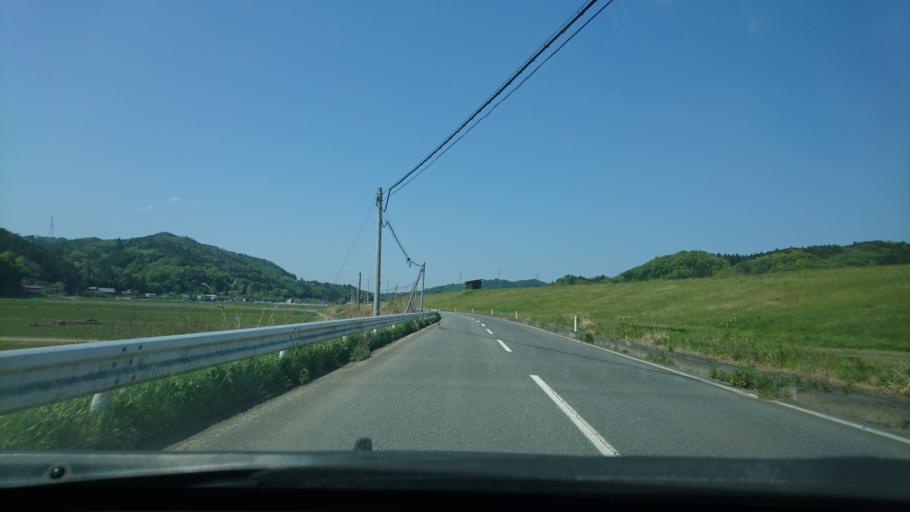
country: JP
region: Iwate
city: Ichinoseki
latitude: 38.9083
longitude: 141.2560
